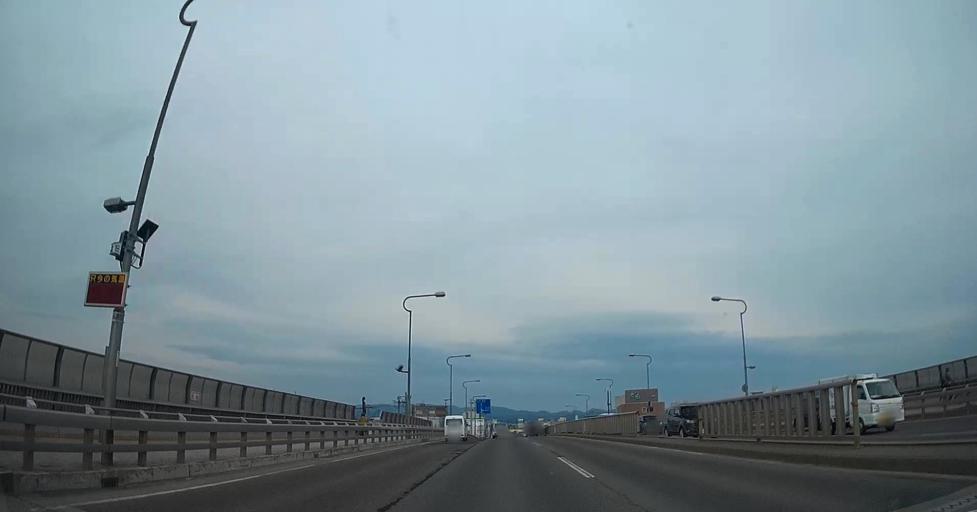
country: JP
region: Aomori
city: Aomori Shi
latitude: 40.8249
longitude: 140.7318
